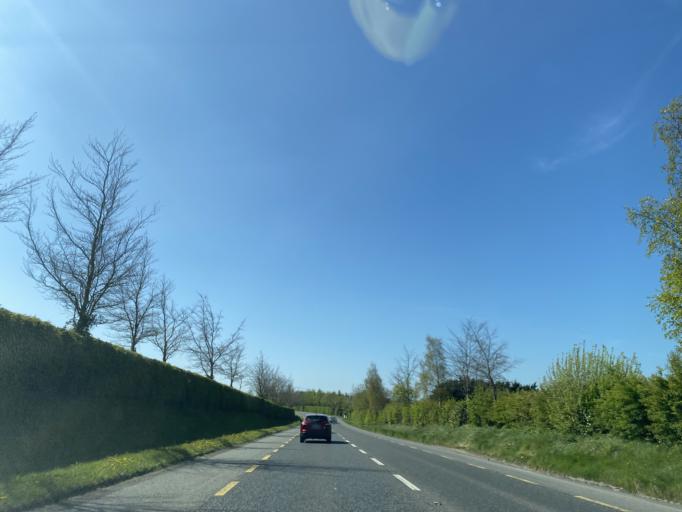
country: IE
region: Leinster
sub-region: Kildare
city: Maynooth
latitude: 53.3351
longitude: -6.6054
